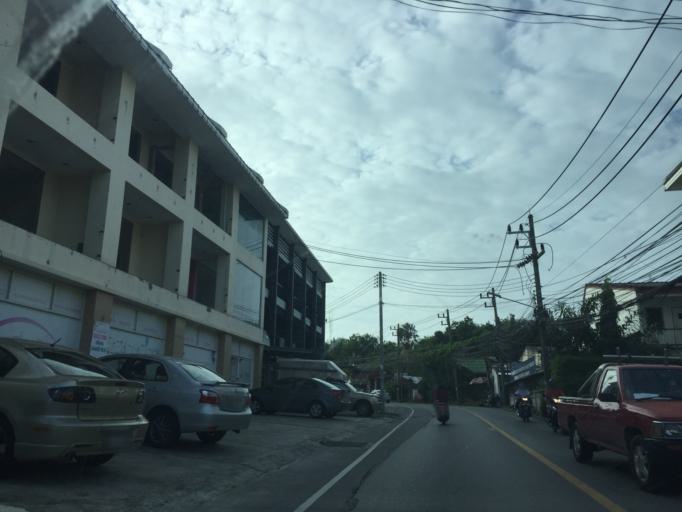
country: TH
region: Phuket
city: Mueang Phuket
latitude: 7.8625
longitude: 98.3706
